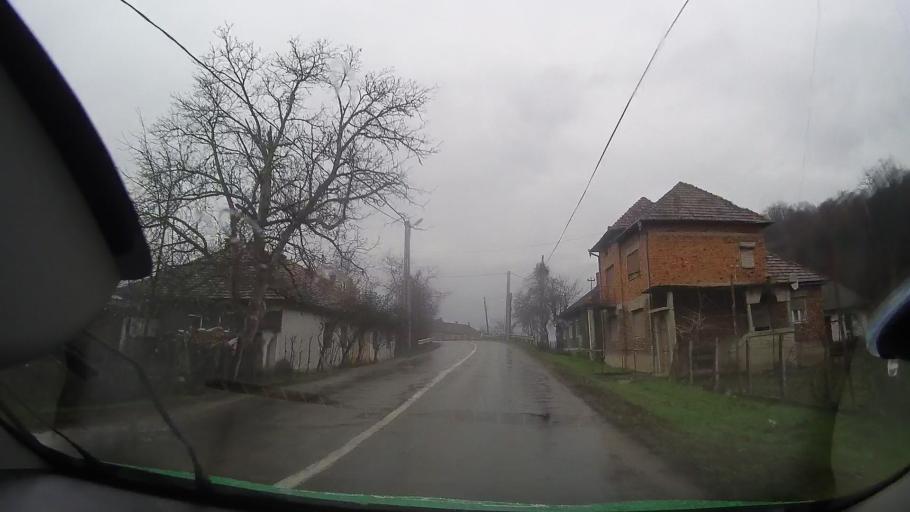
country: RO
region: Bihor
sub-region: Comuna Holod
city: Holod
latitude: 46.7789
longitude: 22.1344
